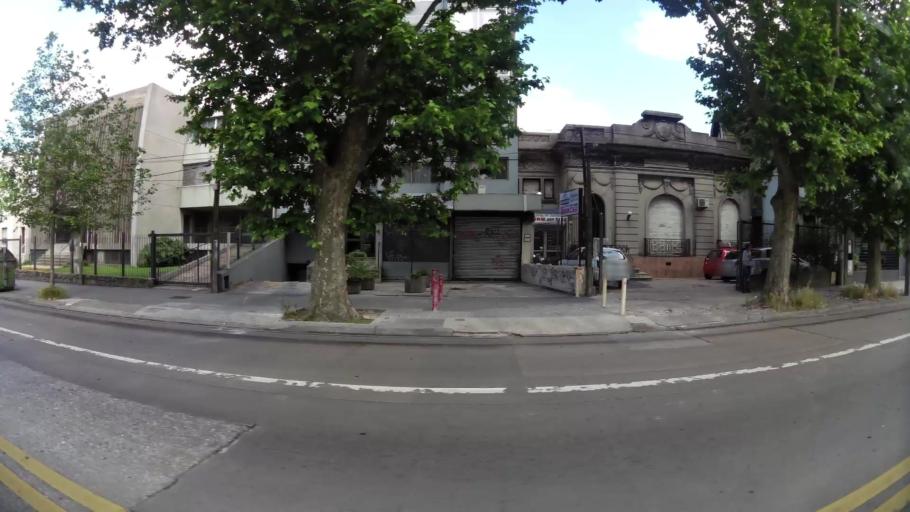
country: UY
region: Montevideo
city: Montevideo
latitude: -34.8832
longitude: -56.1545
